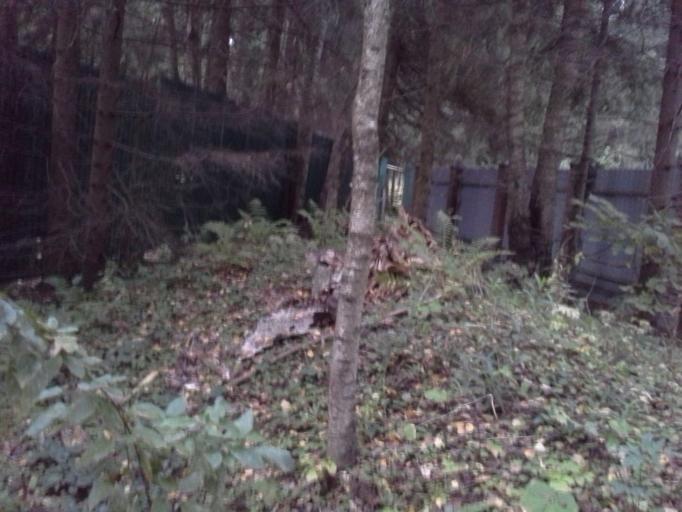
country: RU
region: Moskovskaya
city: Krasnoznamensk
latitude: 55.6170
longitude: 37.0725
